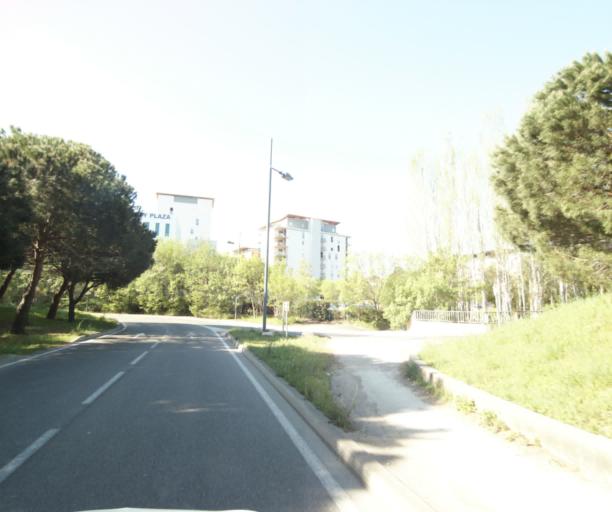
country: FR
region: Languedoc-Roussillon
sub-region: Departement de l'Herault
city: Castelnau-le-Lez
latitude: 43.6086
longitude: 3.9117
